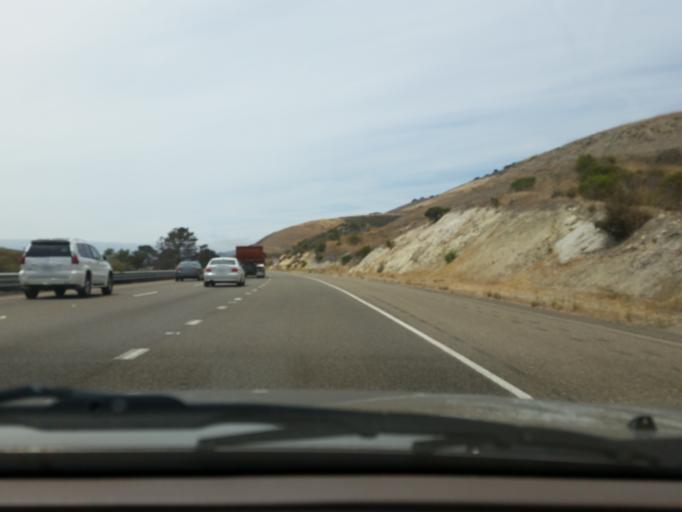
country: US
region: California
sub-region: San Luis Obispo County
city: Pismo Beach
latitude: 35.1490
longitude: -120.6483
